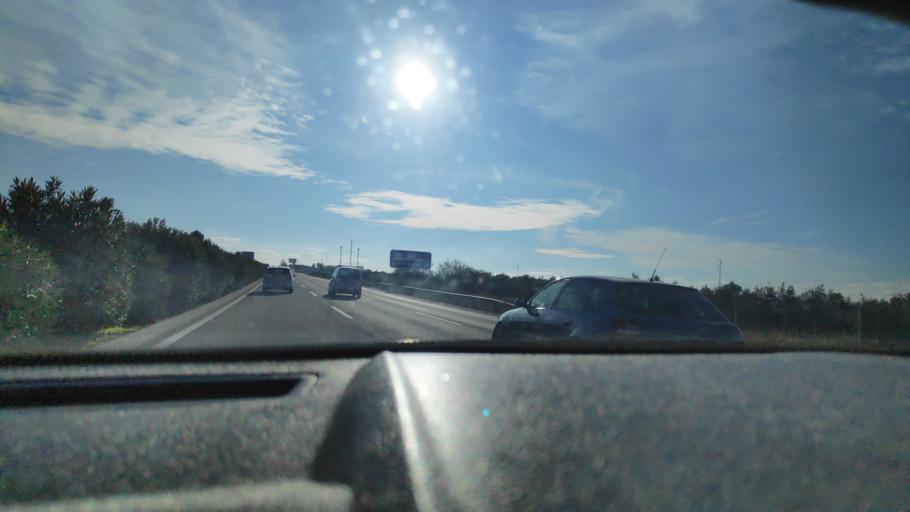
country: ES
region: Andalusia
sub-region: Province of Cordoba
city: La Carlota
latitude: 37.5972
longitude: -4.9759
